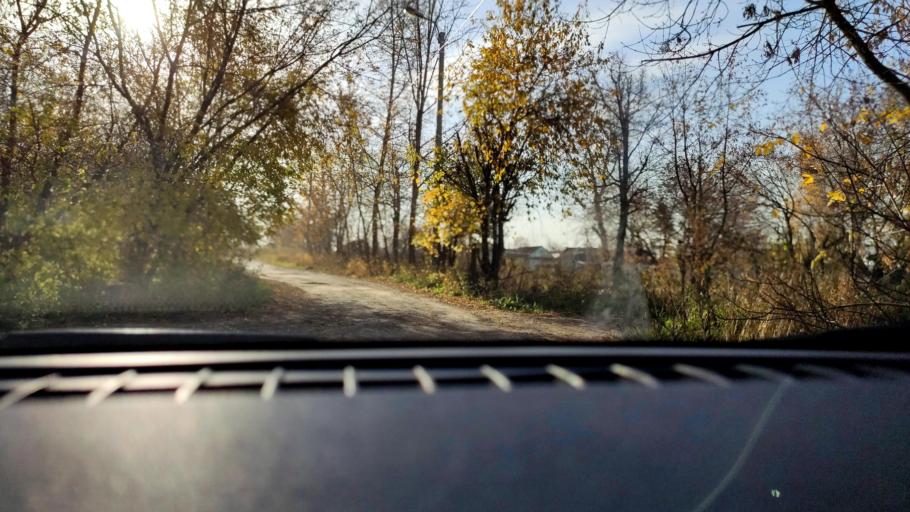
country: RU
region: Perm
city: Perm
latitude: 58.0316
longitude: 56.3187
